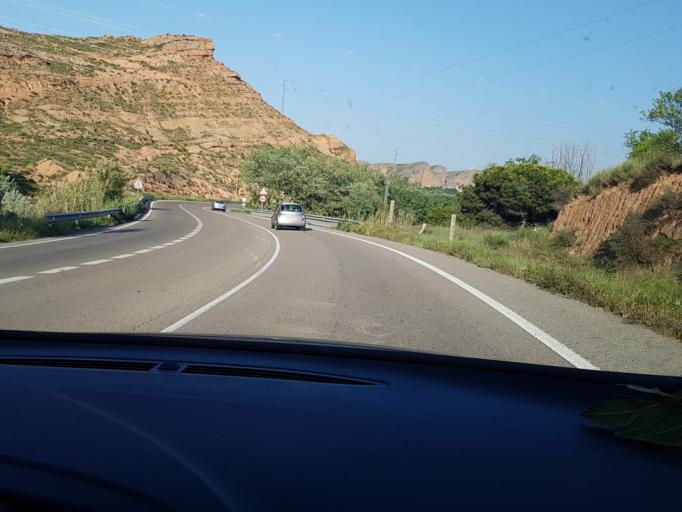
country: ES
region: La Rioja
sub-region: Provincia de La Rioja
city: Arnedo
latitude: 42.2328
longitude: -2.0804
